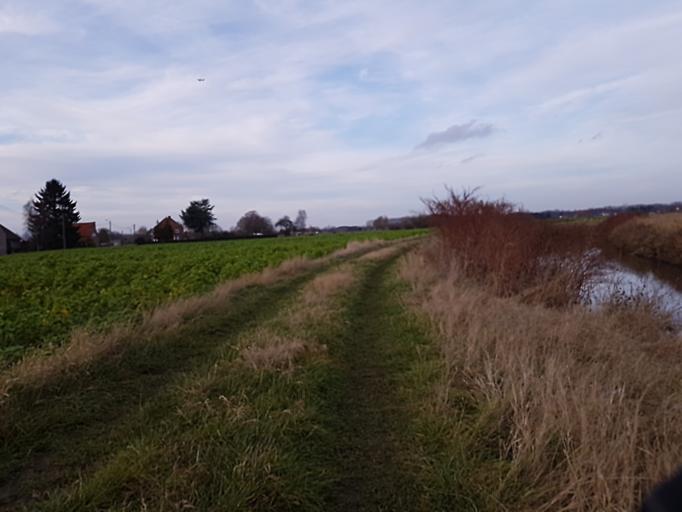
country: BE
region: Flanders
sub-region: Provincie Vlaams-Brabant
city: Rotselaar
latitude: 50.9490
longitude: 4.7014
